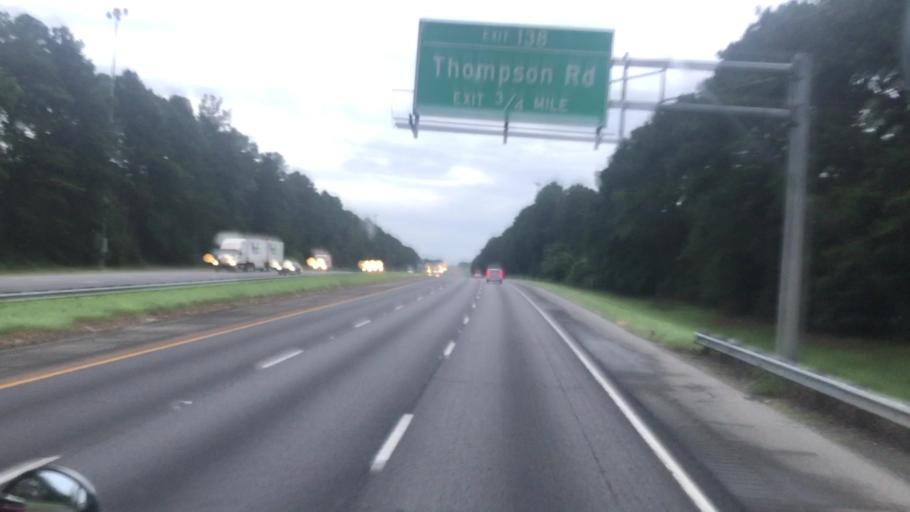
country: US
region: Georgia
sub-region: Houston County
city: Perry
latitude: 32.4794
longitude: -83.7422
